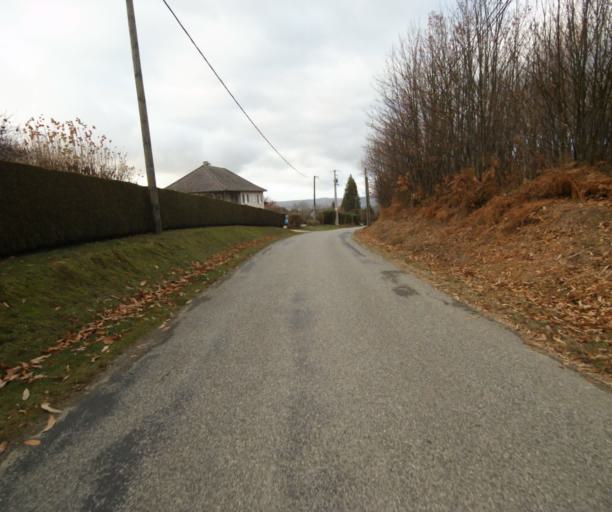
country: FR
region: Limousin
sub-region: Departement de la Correze
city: Sainte-Fortunade
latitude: 45.2064
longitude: 1.7801
